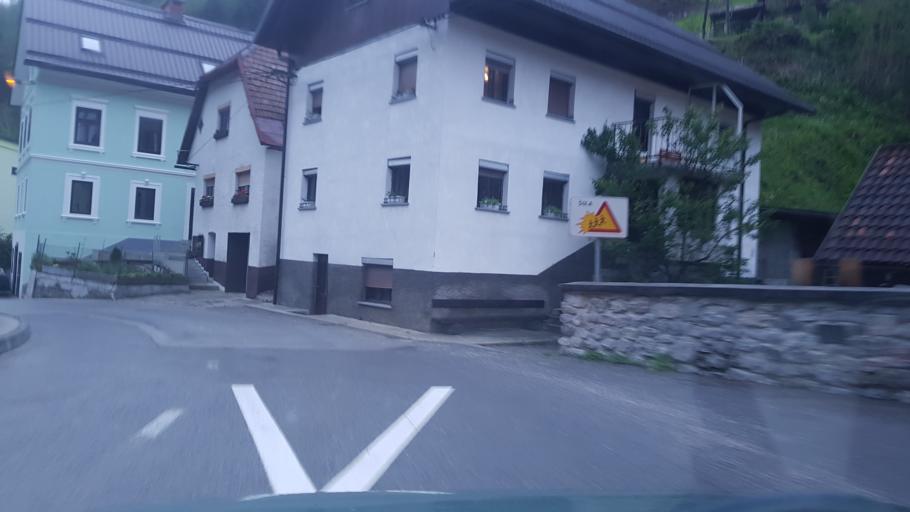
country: SI
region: Bohinj
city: Bohinjska Bistrica
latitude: 46.2145
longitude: 13.9739
